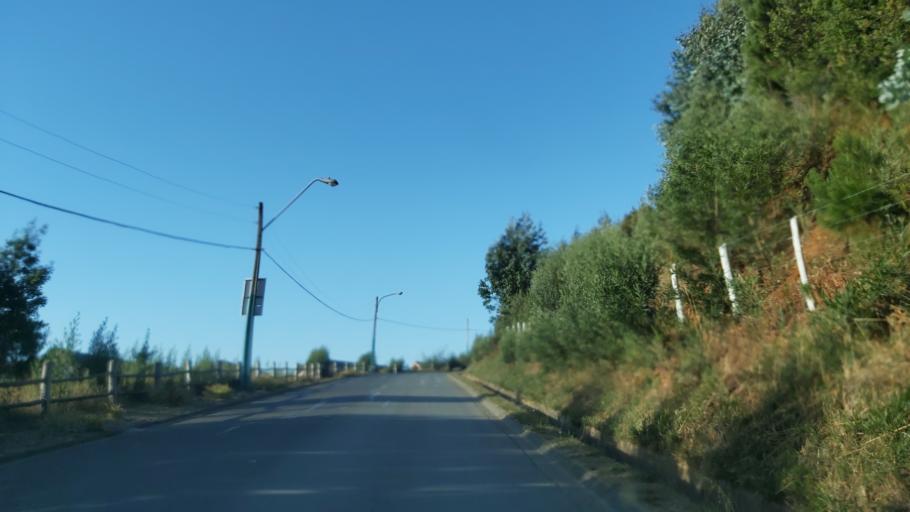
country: CL
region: Biobio
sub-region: Provincia de Concepcion
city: Tome
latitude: -36.5354
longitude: -72.9274
